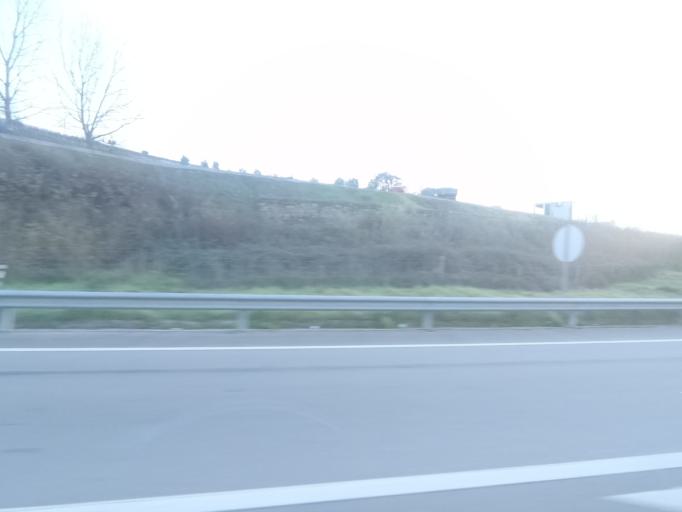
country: PT
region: Vila Real
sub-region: Peso da Regua
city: Peso da Regua
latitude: 41.1622
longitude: -7.7875
